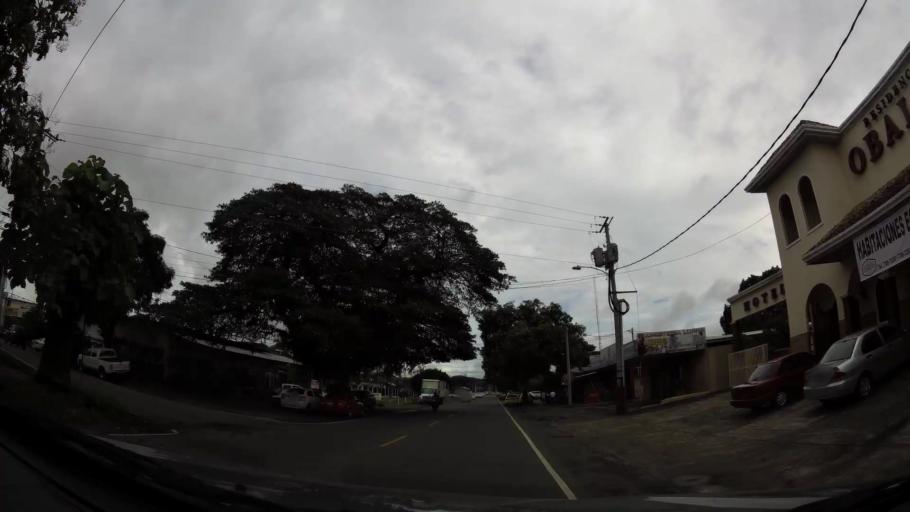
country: PA
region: Chiriqui
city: David
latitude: 8.4420
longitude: -82.4232
